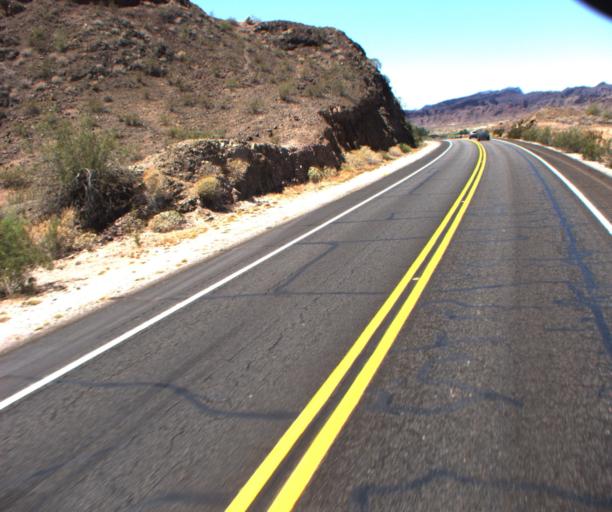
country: US
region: Arizona
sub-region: La Paz County
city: Cienega Springs
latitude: 34.2568
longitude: -114.1481
